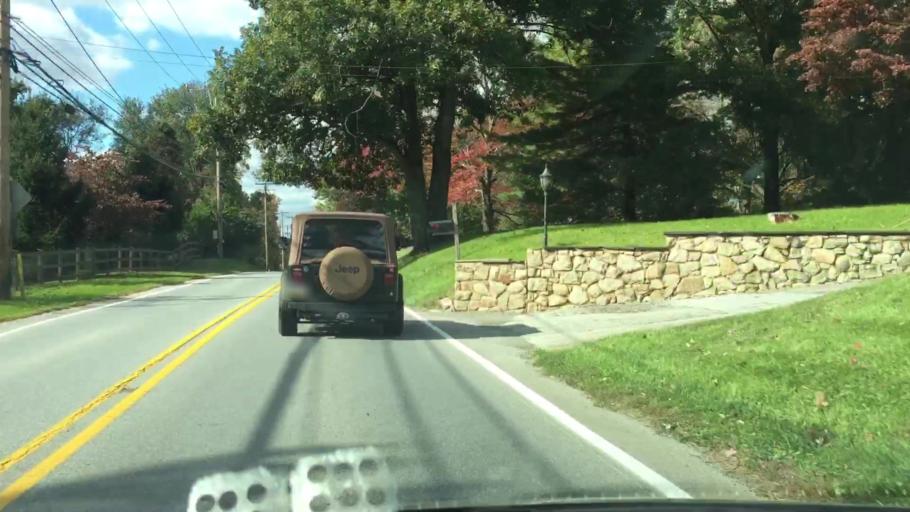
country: US
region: Pennsylvania
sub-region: Chester County
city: West Chester
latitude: 39.9959
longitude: -75.5621
